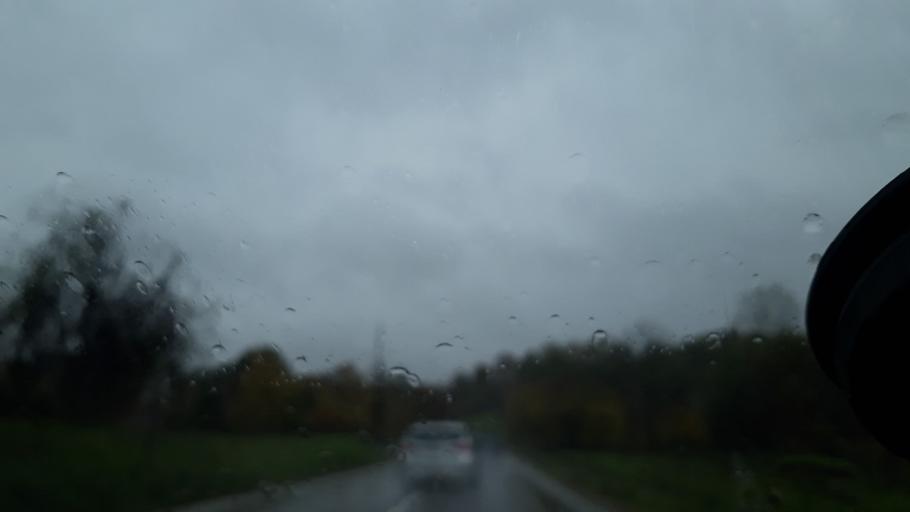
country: BA
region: Republika Srpska
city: Maglajani
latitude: 44.8677
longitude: 17.4678
